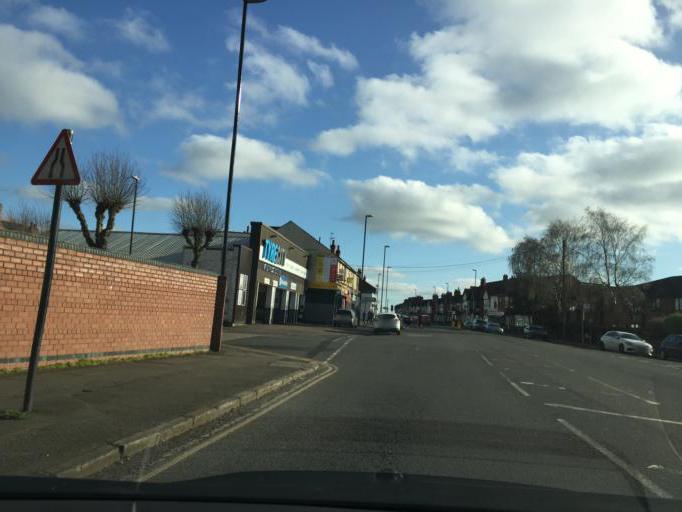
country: GB
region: England
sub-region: Coventry
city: Coventry
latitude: 52.4046
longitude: -1.4867
